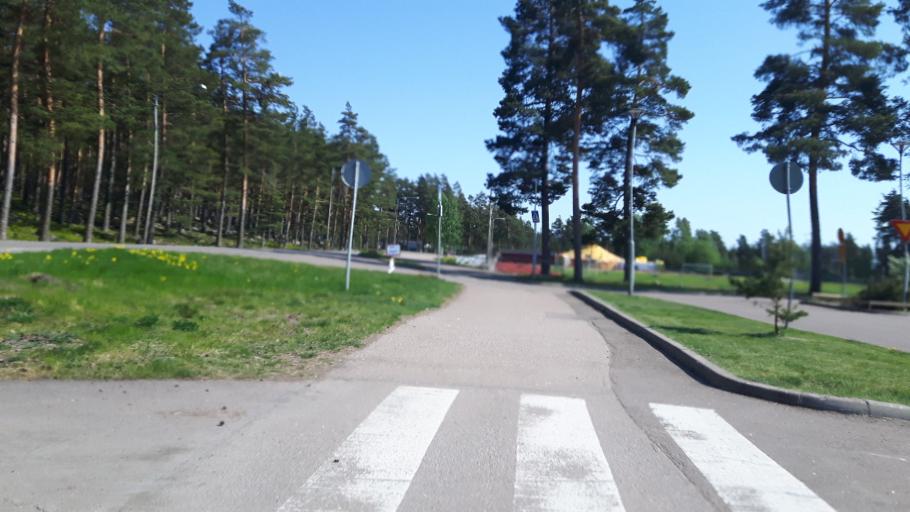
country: FI
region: Kymenlaakso
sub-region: Kotka-Hamina
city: Broby
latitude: 60.4890
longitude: 26.7467
